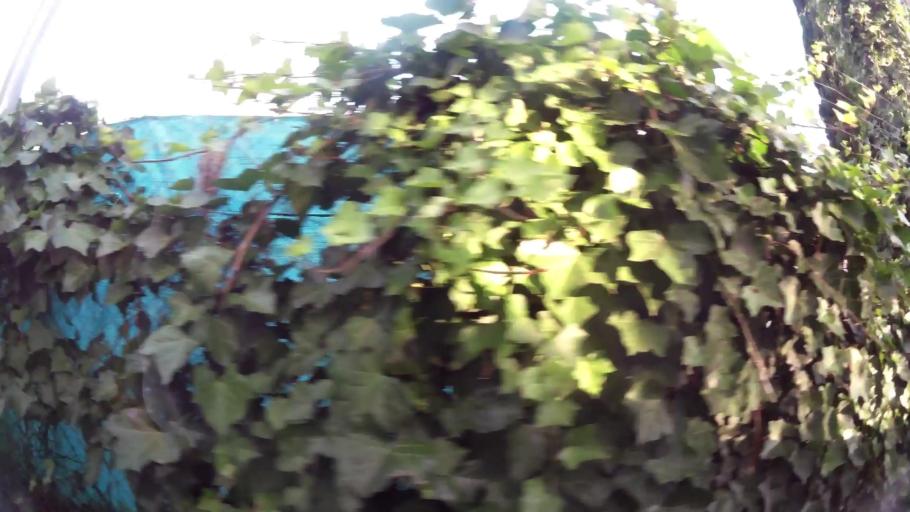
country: AR
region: Buenos Aires
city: Santa Catalina - Dique Lujan
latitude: -34.4521
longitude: -58.6590
